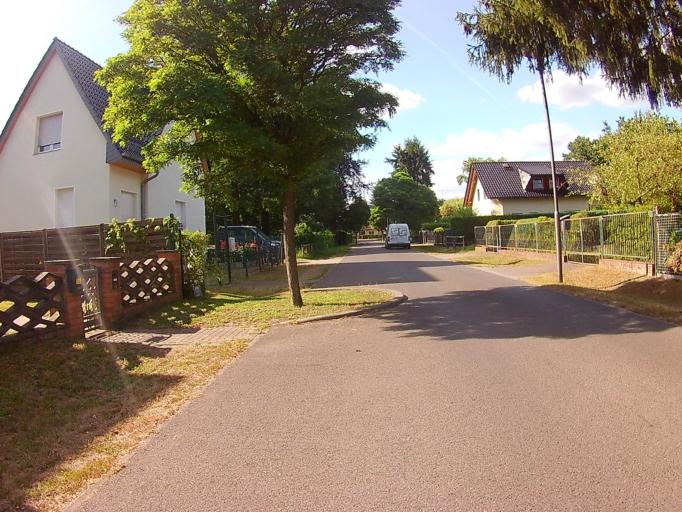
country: DE
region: Brandenburg
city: Zeuthen
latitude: 52.3658
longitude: 13.6114
